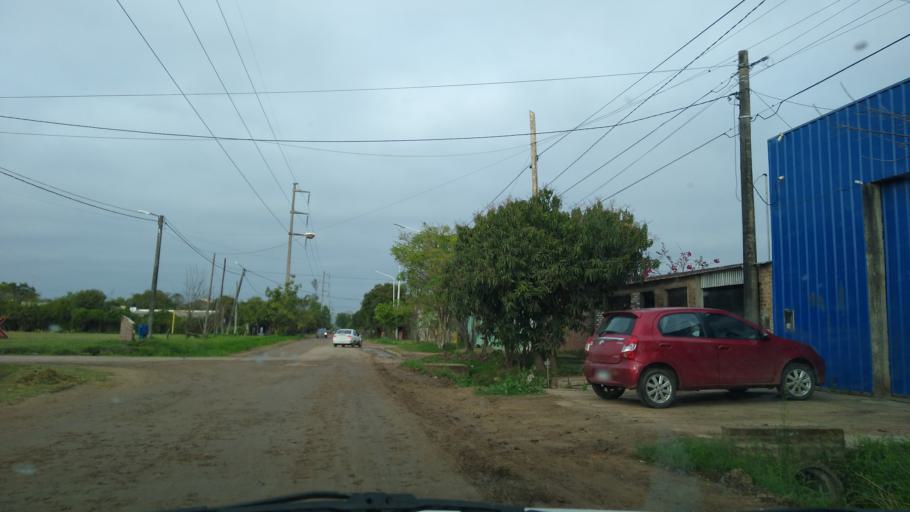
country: AR
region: Chaco
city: Barranqueras
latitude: -27.4873
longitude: -58.9413
